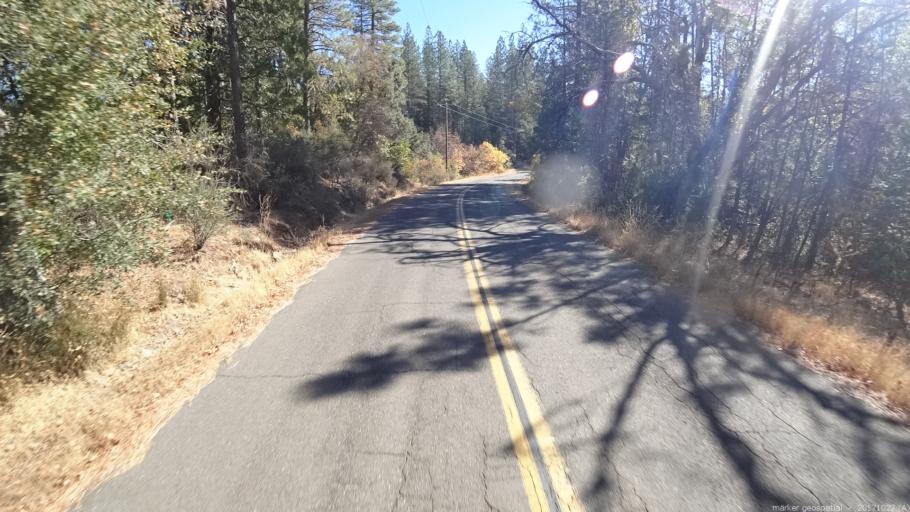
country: US
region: California
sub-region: Shasta County
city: Shingletown
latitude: 40.7516
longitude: -121.9501
